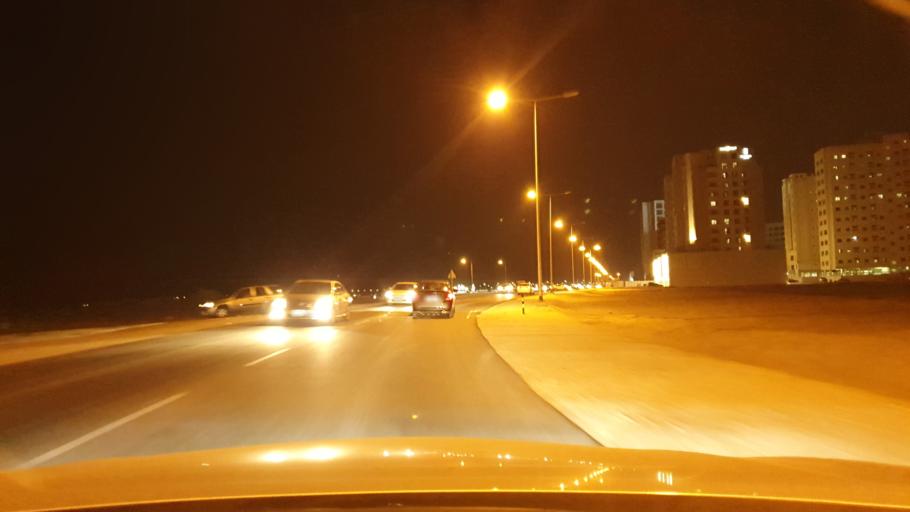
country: BH
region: Muharraq
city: Al Muharraq
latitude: 26.2612
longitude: 50.5946
